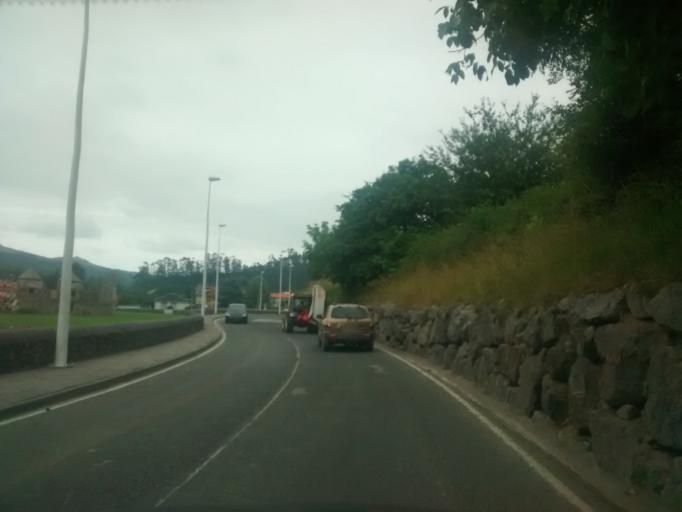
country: ES
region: Cantabria
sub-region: Provincia de Cantabria
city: Luzmela
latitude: 43.3150
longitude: -4.1930
